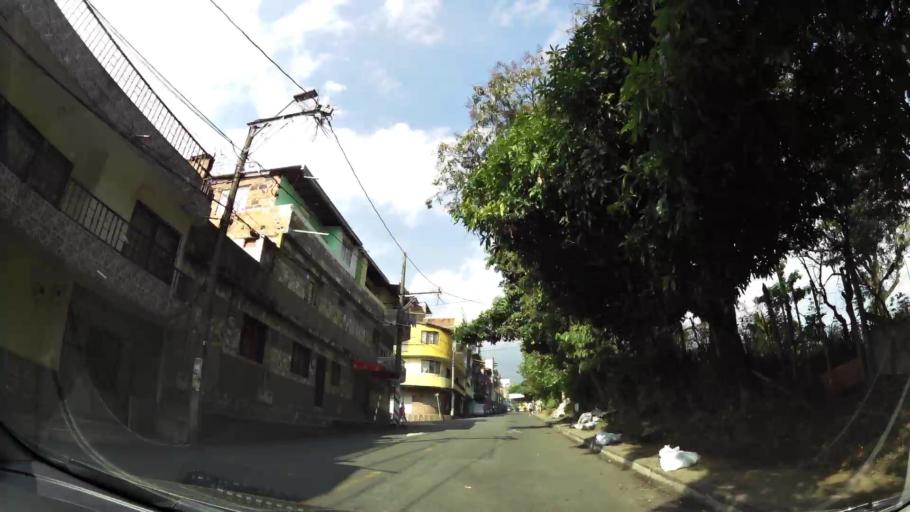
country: CO
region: Antioquia
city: La Estrella
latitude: 6.1722
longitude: -75.6394
